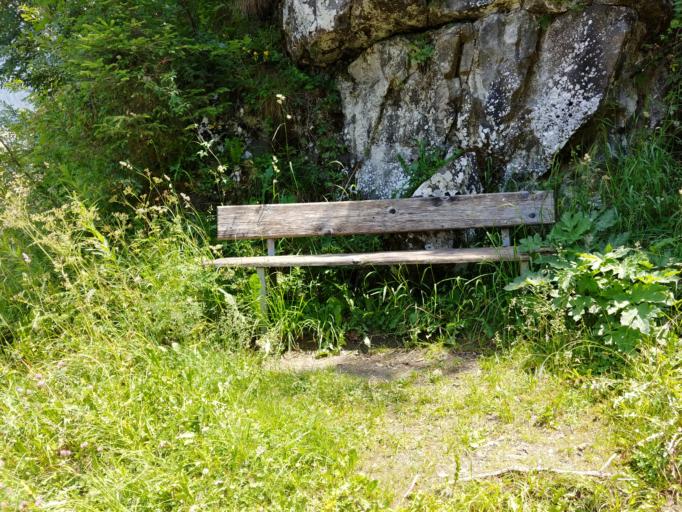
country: IT
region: Trentino-Alto Adige
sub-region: Bolzano
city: Santa Cristina Valgardena
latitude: 46.5557
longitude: 11.7192
